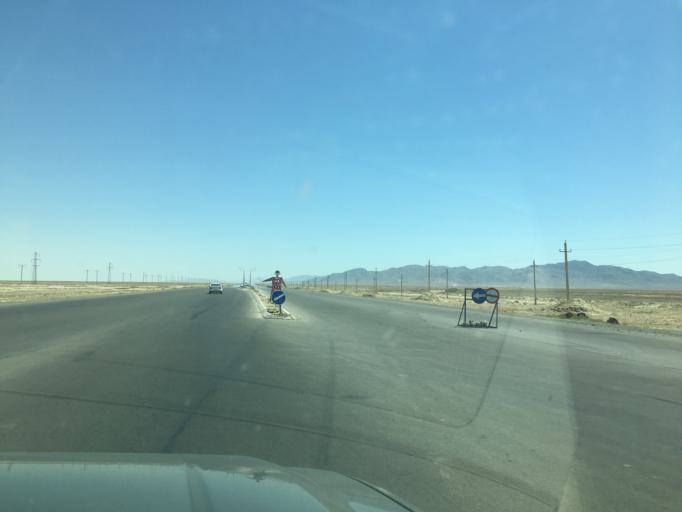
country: TM
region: Balkan
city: Gazanjyk
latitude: 39.1292
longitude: 55.8921
